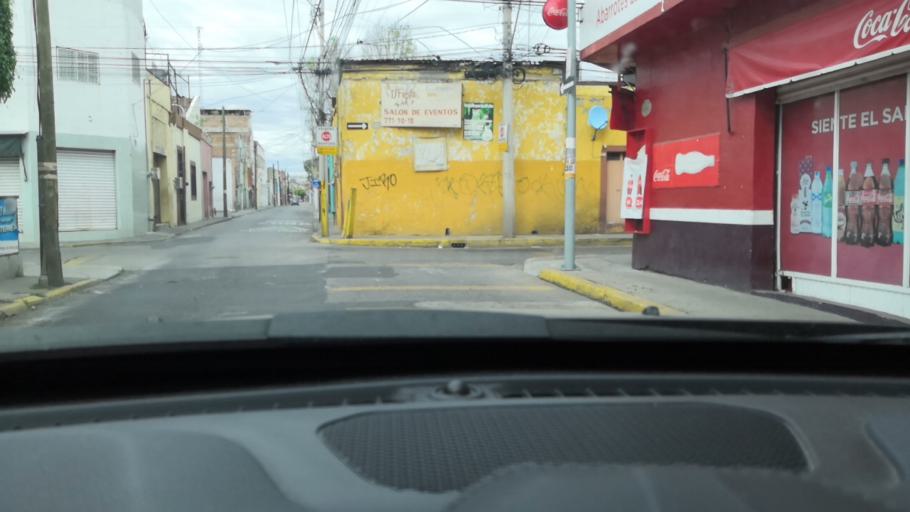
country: MX
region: Guanajuato
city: Leon
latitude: 21.1176
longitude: -101.6771
